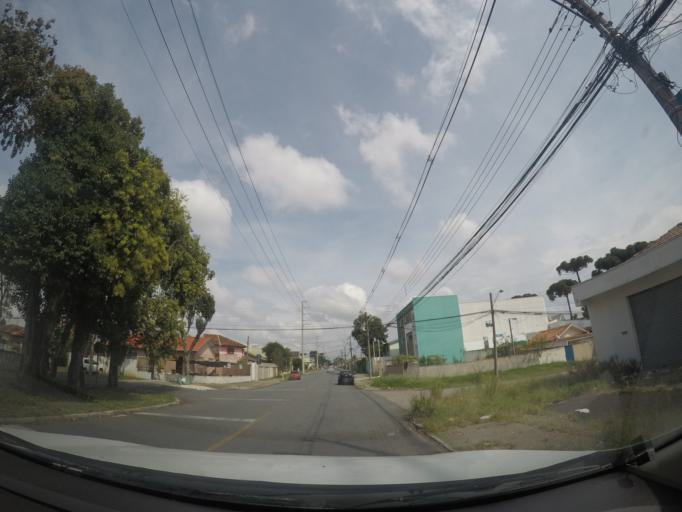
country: BR
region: Parana
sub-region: Curitiba
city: Curitiba
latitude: -25.4757
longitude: -49.2629
